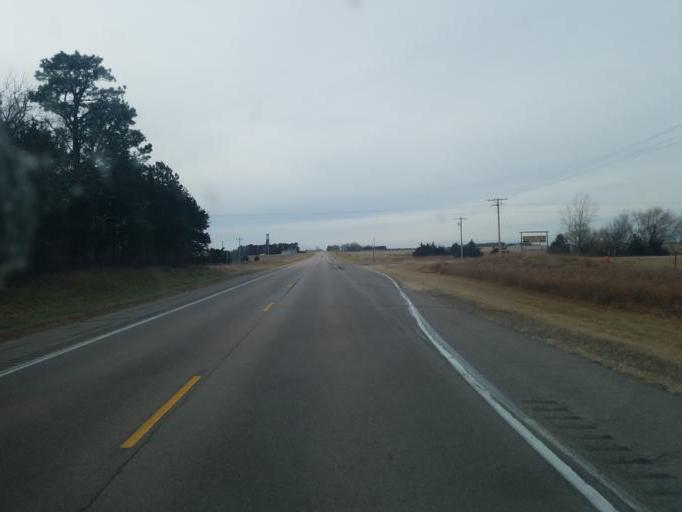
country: US
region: Nebraska
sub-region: Antelope County
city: Neligh
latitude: 42.3351
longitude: -98.1640
